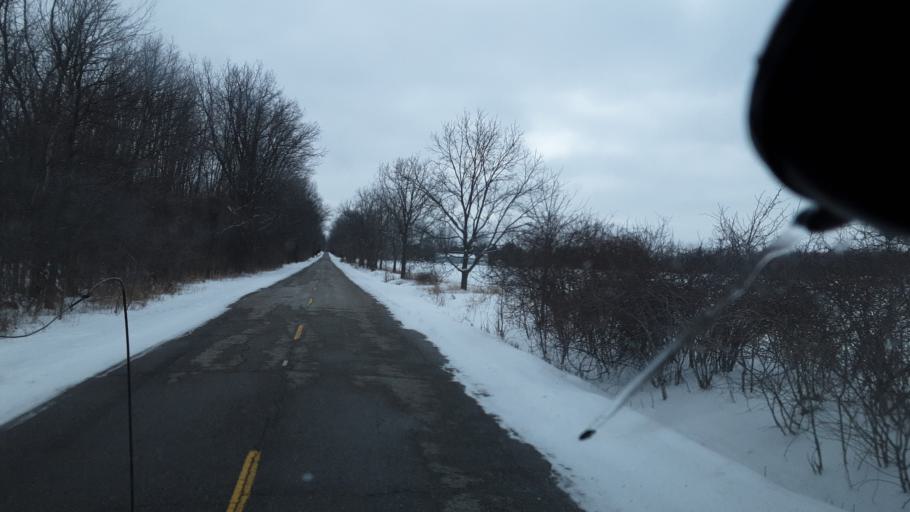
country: US
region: Michigan
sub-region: Ingham County
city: Mason
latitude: 42.5496
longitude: -84.4036
